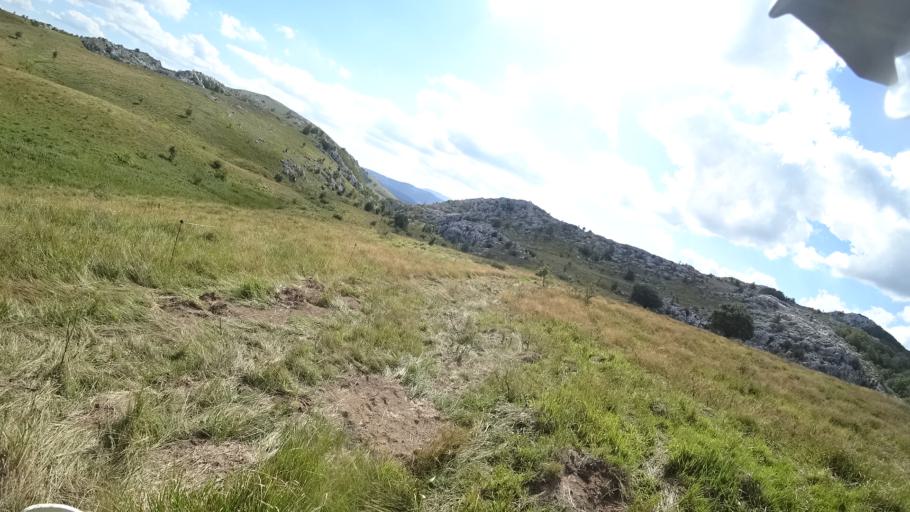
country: HR
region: Zadarska
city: Gracac
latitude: 44.4120
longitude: 16.0005
